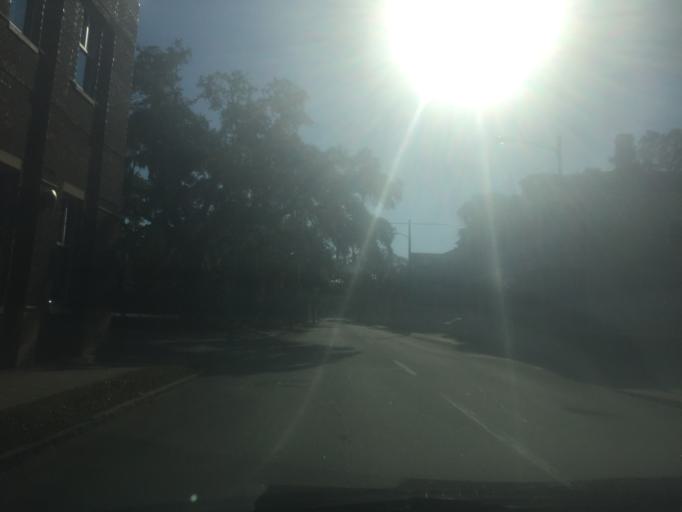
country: US
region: Georgia
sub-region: Chatham County
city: Savannah
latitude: 32.0610
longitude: -81.0999
